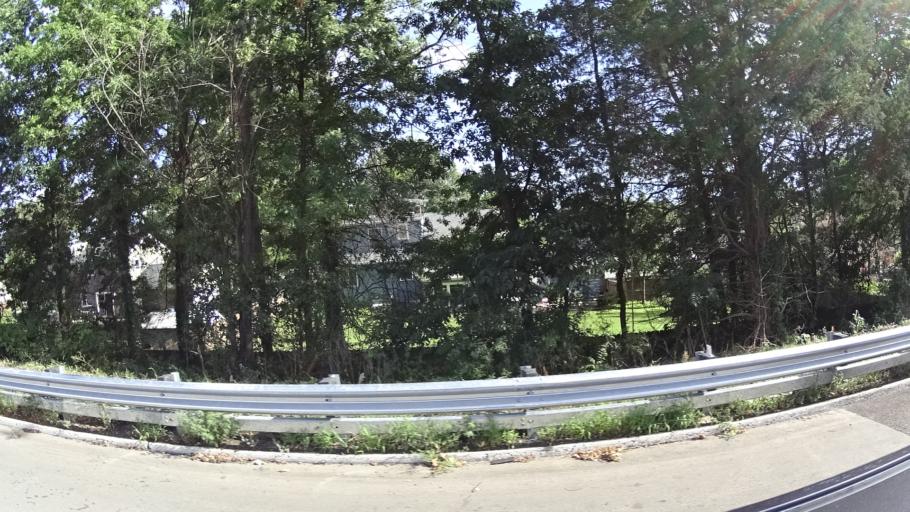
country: US
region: New Jersey
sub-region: Somerset County
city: Bound Brook
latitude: 40.5757
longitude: -74.5475
